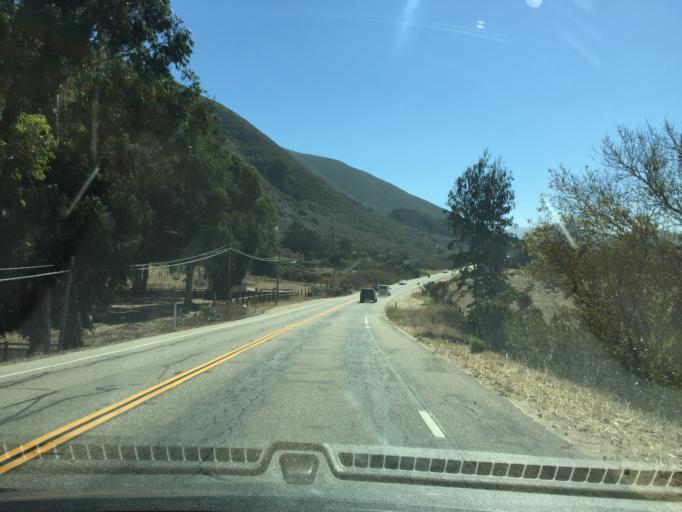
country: US
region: California
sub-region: Monterey County
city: Carmel-by-the-Sea
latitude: 36.3991
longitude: -121.9043
